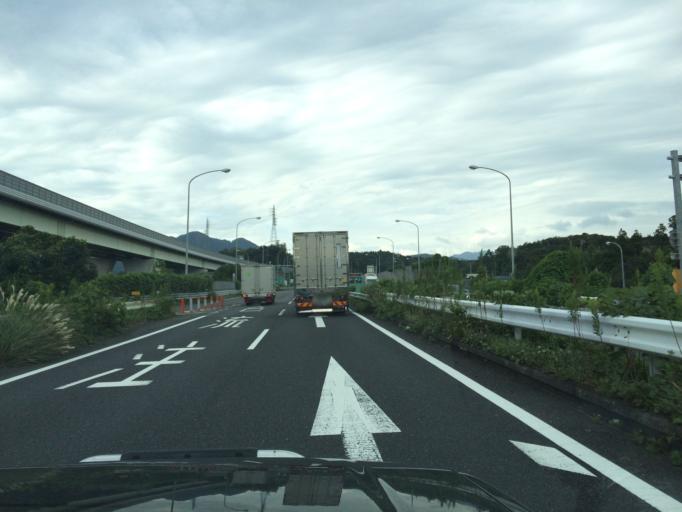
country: JP
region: Mie
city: Kameyama
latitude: 34.8579
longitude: 136.4144
